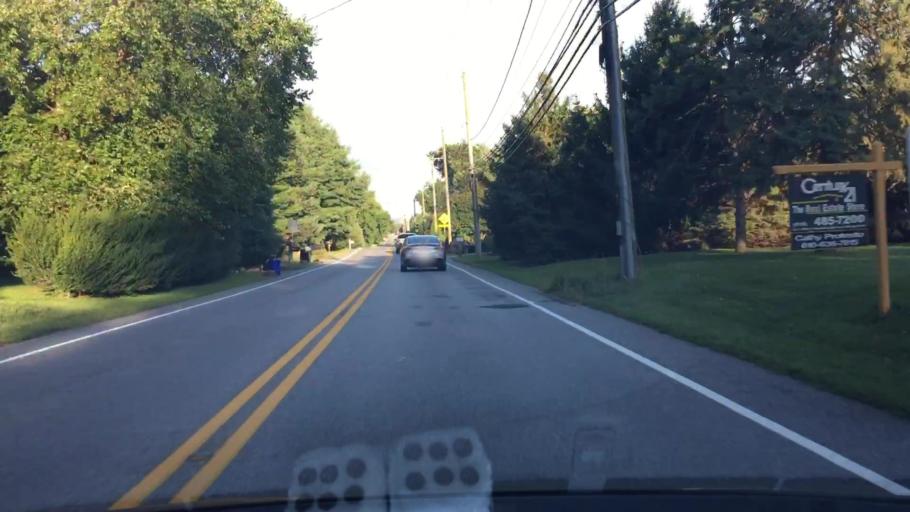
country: US
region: Delaware
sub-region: New Castle County
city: Claymont
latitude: 39.8388
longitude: -75.4916
